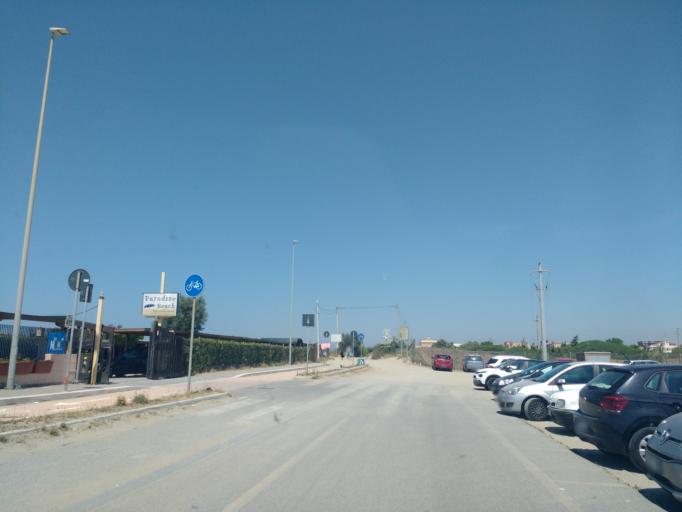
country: IT
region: Latium
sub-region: Citta metropolitana di Roma Capitale
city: Passo Oscuro
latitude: 41.8934
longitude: 12.1641
